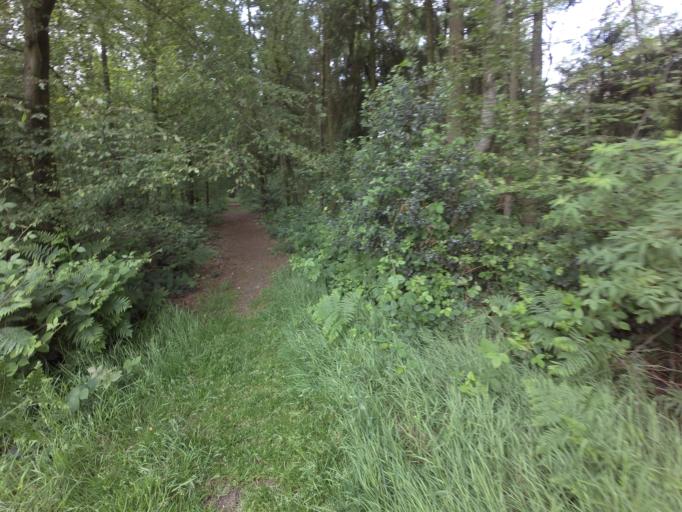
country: BE
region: Wallonia
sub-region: Province de Liege
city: Plombieres
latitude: 50.7840
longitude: 5.9493
